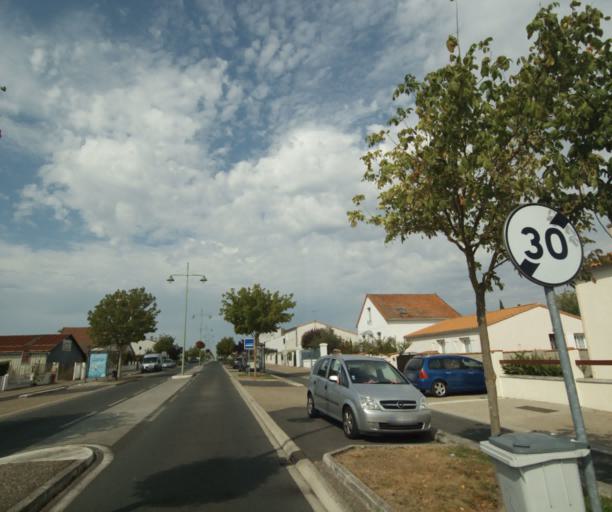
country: FR
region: Poitou-Charentes
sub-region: Departement de la Charente-Maritime
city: Tonnay-Charente
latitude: 45.9464
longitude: -0.9016
